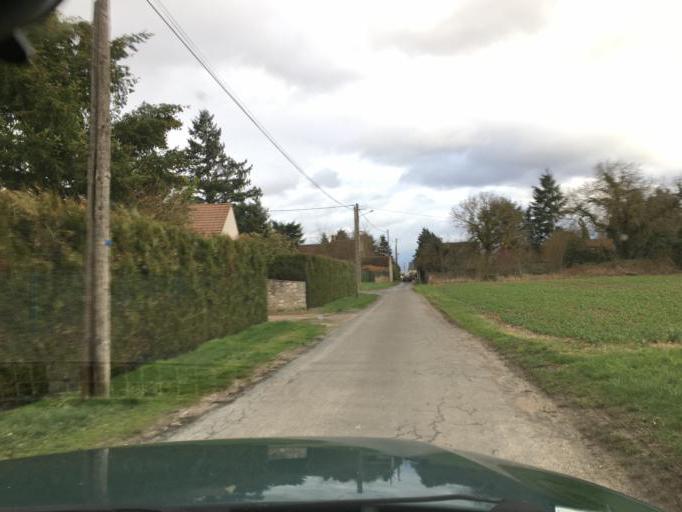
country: FR
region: Centre
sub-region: Departement du Loiret
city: Lailly-en-Val
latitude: 47.7476
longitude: 1.6569
